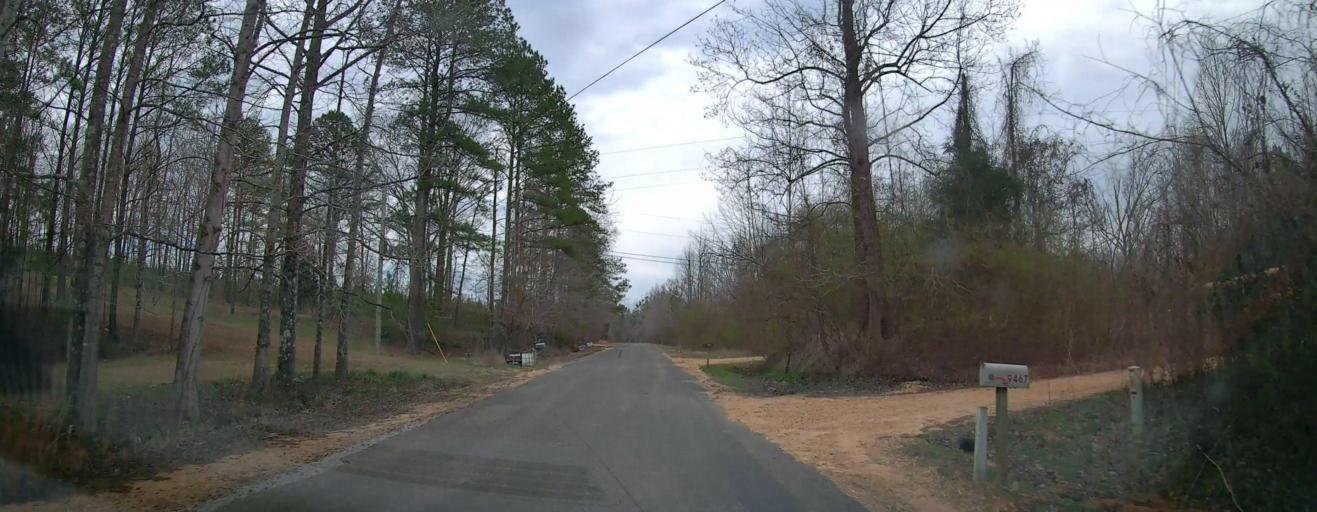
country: US
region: Alabama
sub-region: Marion County
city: Hamilton
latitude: 34.2016
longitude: -88.1888
